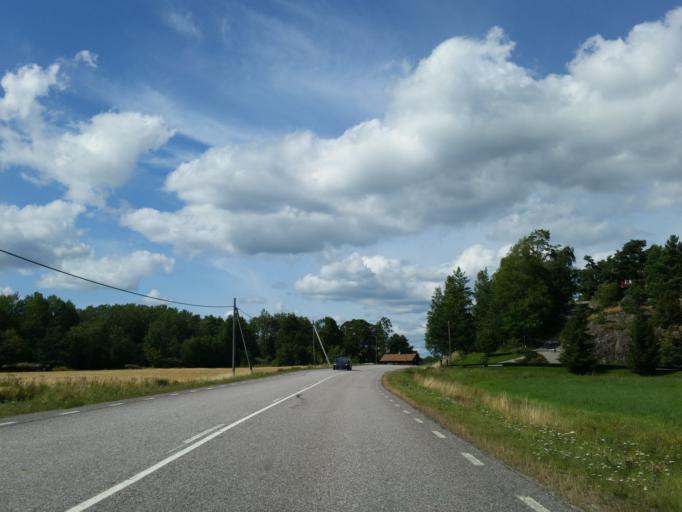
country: SE
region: Soedermanland
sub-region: Trosa Kommun
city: Vagnharad
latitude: 58.9995
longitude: 17.6058
